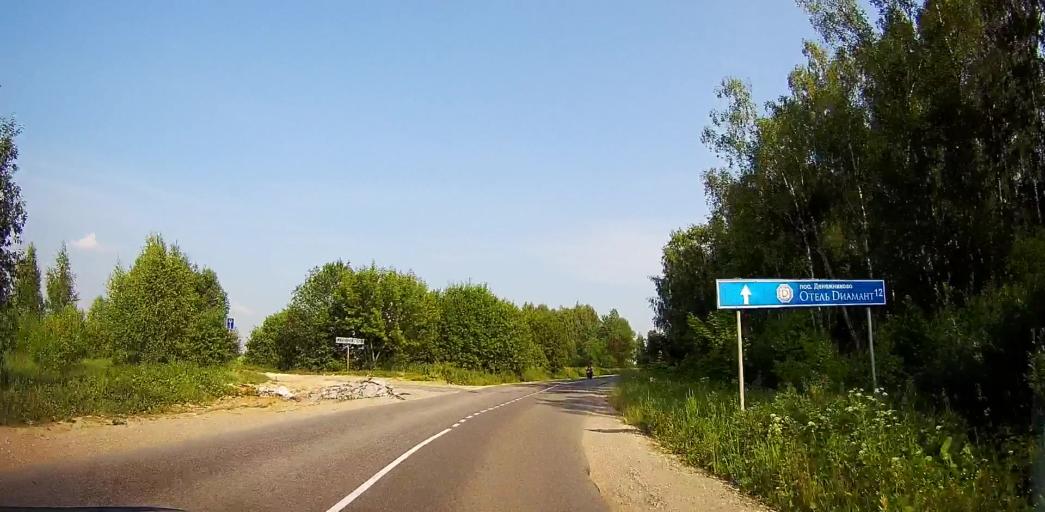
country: RU
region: Moskovskaya
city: Yakovlevskoye
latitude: 55.4319
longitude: 37.9315
